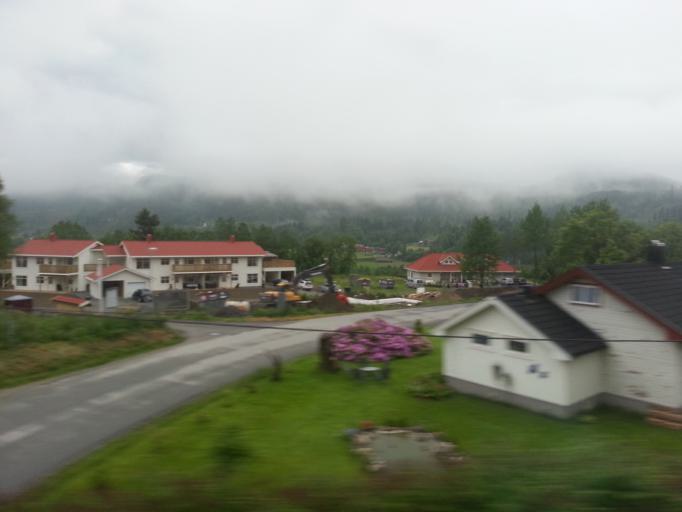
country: NO
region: Sor-Trondelag
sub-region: Midtre Gauldal
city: Storen
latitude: 63.0330
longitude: 10.2701
